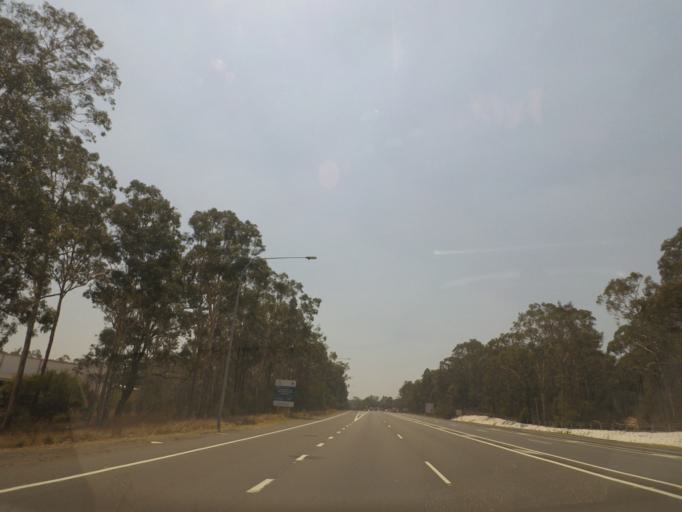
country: AU
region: New South Wales
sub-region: Newcastle
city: Beresfield
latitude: -32.8111
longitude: 151.6428
